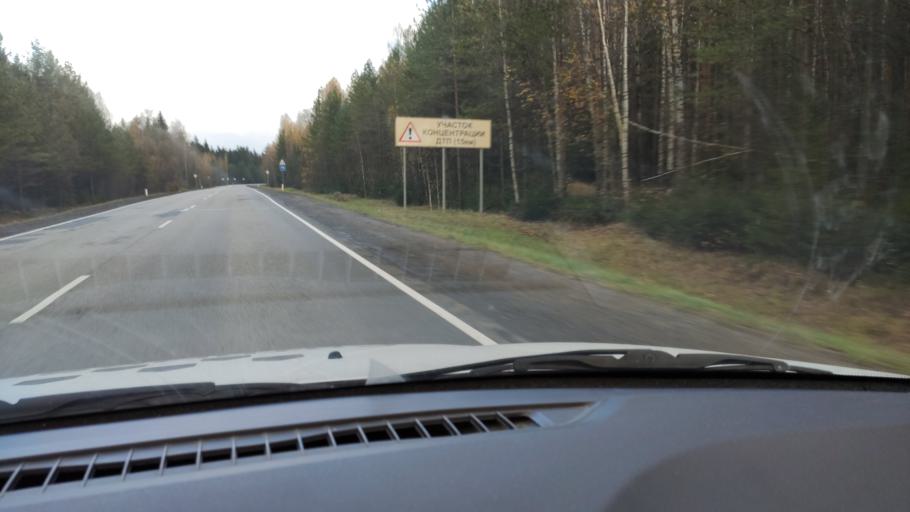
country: RU
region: Kirov
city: Belaya Kholunitsa
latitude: 58.9029
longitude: 50.9376
